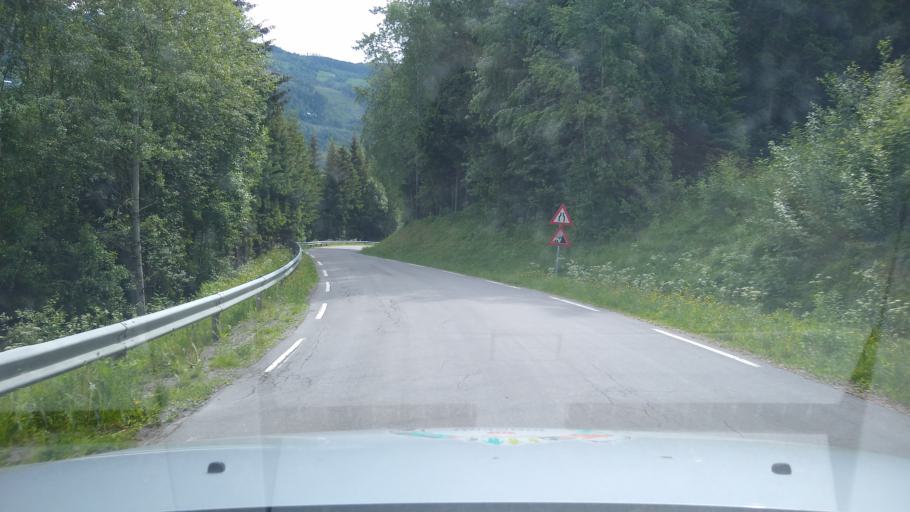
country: NO
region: Oppland
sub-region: Ringebu
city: Ringebu
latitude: 61.5195
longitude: 10.1356
